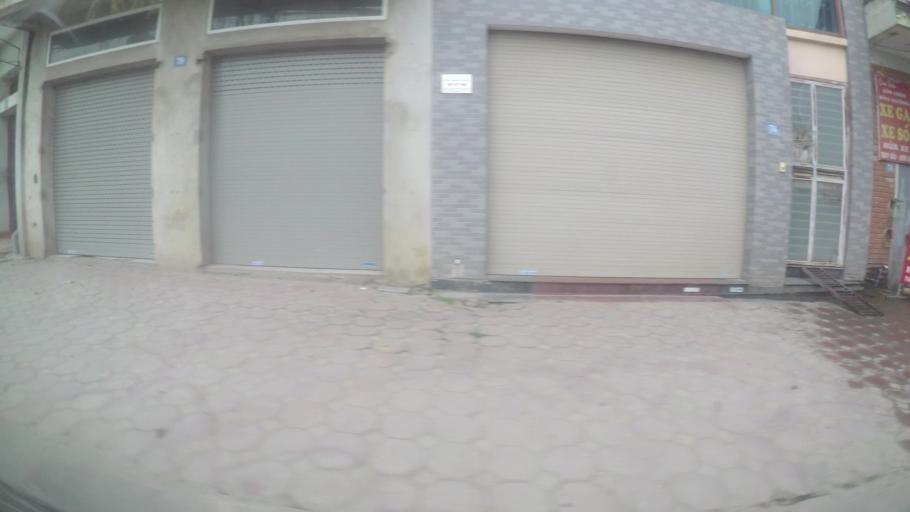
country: VN
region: Ha Noi
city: Cau Dien
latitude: 21.0377
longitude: 105.7419
